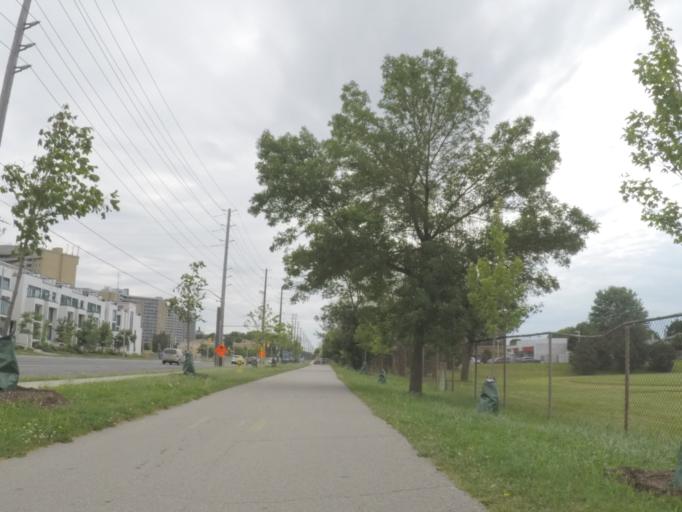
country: CA
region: Ontario
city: Etobicoke
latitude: 43.6750
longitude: -79.5597
